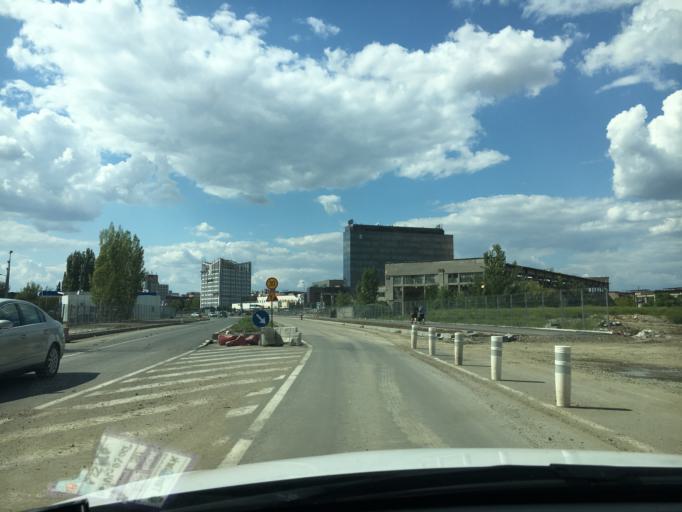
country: RO
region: Timis
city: Timisoara
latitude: 45.7645
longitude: 21.2349
